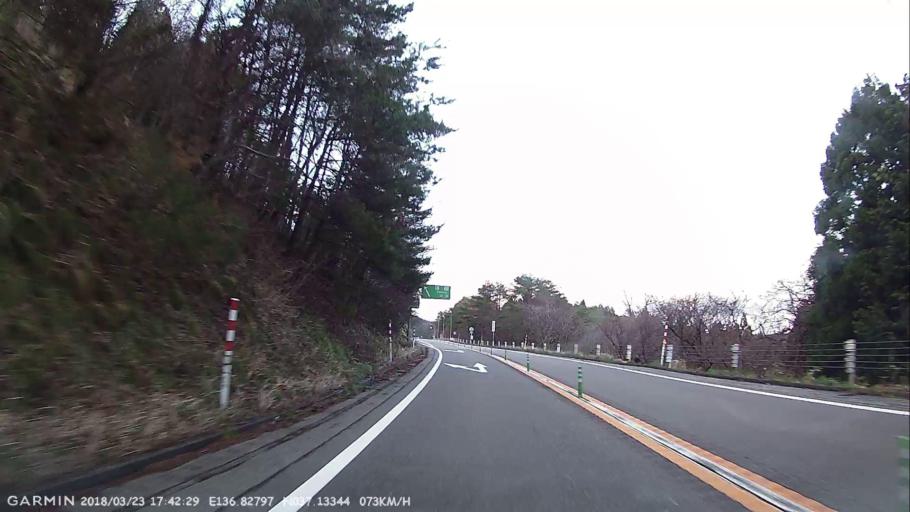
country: JP
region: Ishikawa
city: Nanao
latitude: 37.1335
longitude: 136.8281
